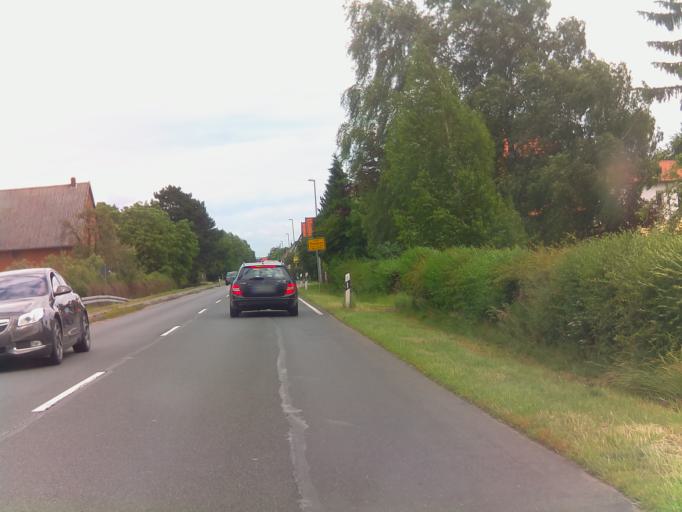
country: DE
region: Lower Saxony
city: Springe
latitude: 52.1729
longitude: 9.6433
